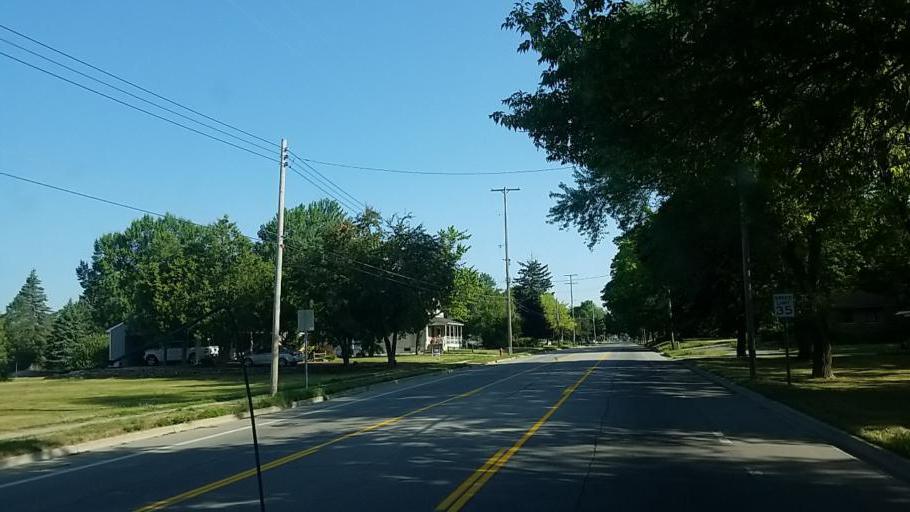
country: US
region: Michigan
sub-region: Newaygo County
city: Fremont
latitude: 43.4611
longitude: -85.9399
